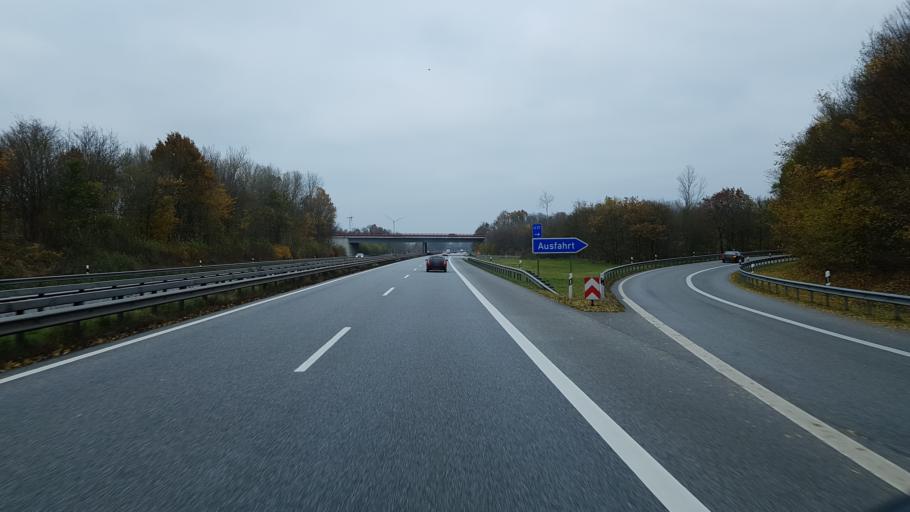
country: DE
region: Lower Saxony
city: Driftsethe
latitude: 53.4394
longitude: 8.5826
